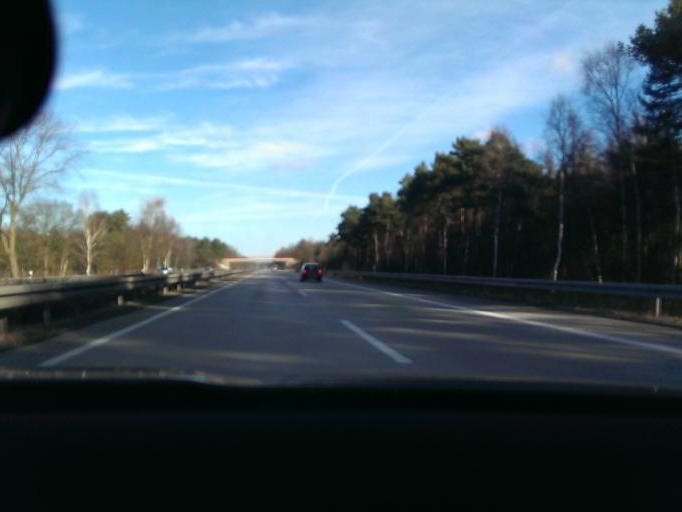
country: DE
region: Lower Saxony
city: Elze
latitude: 52.5271
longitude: 9.7853
